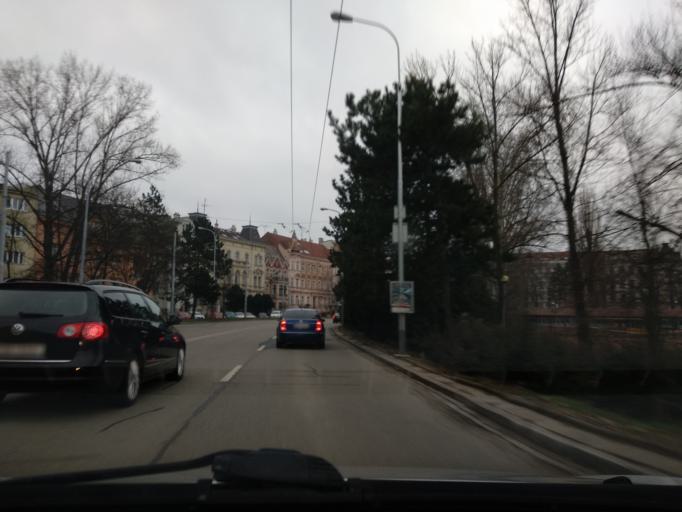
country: CZ
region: South Moravian
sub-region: Mesto Brno
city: Brno
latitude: 49.2064
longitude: 16.6124
